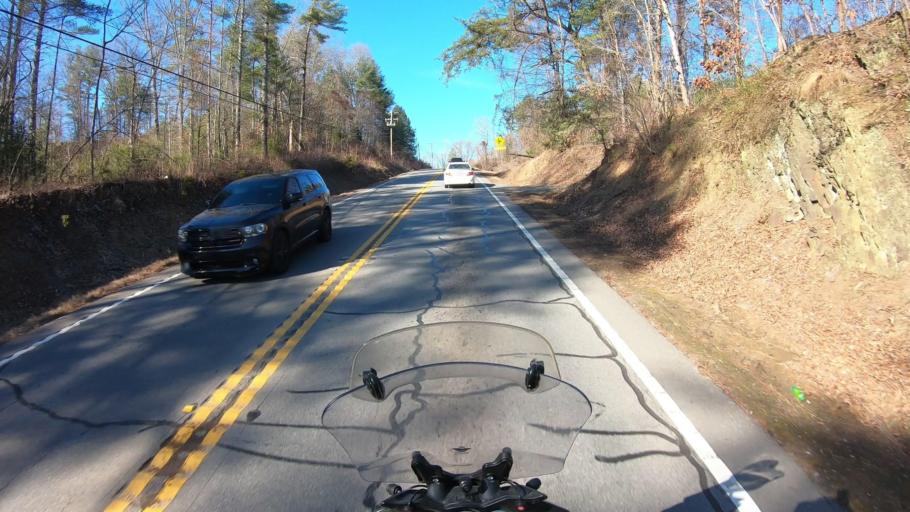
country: US
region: Georgia
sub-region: Fannin County
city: Blue Ridge
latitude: 34.9222
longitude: -84.2832
